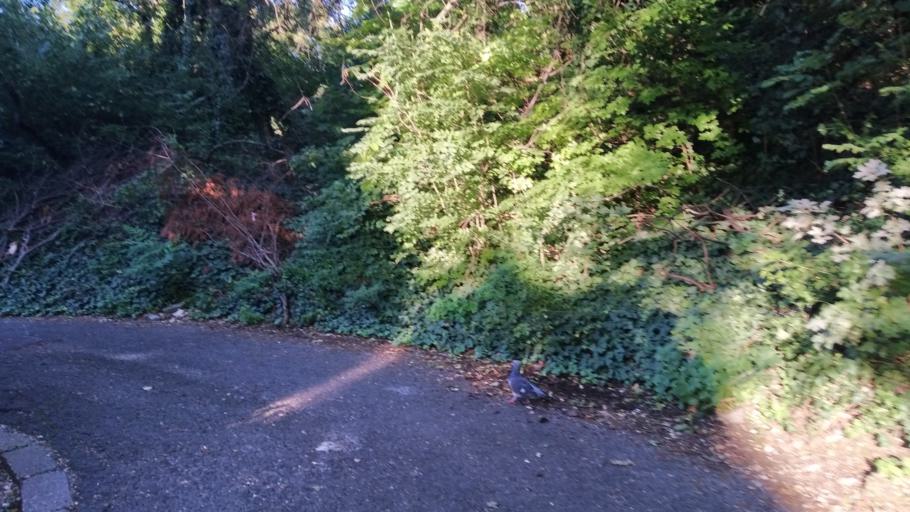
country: HU
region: Budapest
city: Budapest II. keruelet
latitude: 47.5276
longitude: 19.0218
